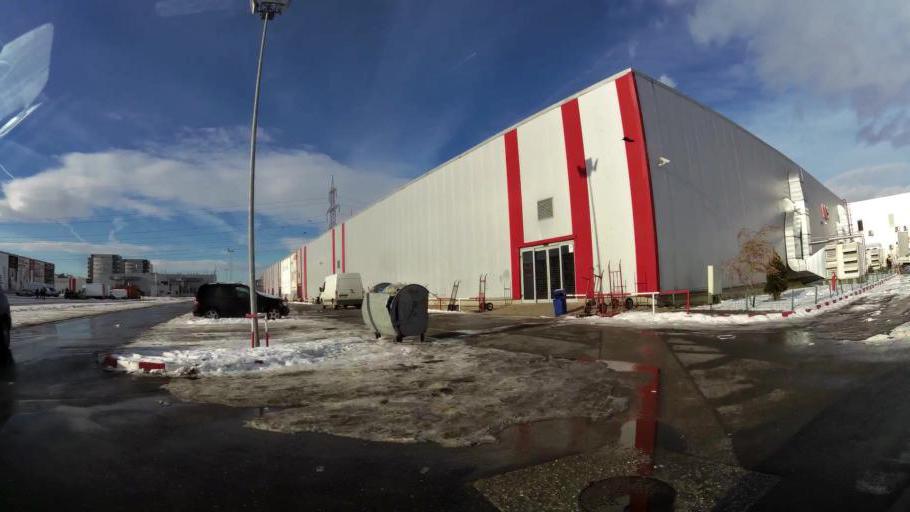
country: RO
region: Ilfov
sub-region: Voluntari City
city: Voluntari
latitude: 44.4750
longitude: 26.1831
